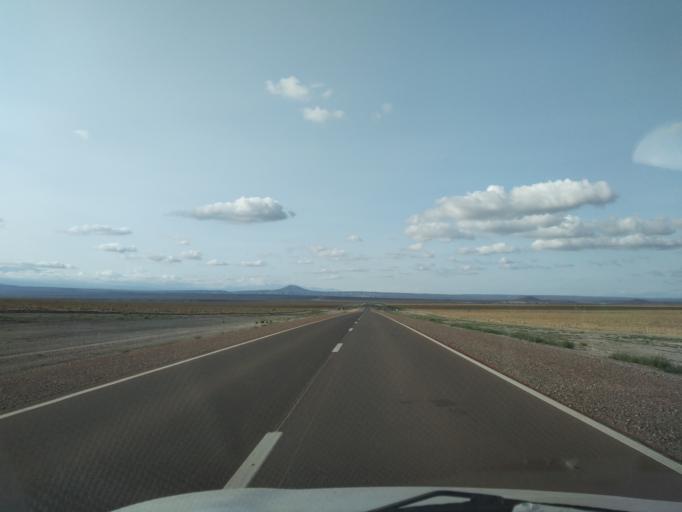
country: AR
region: Mendoza
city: San Rafael
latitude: -34.6798
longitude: -69.1587
